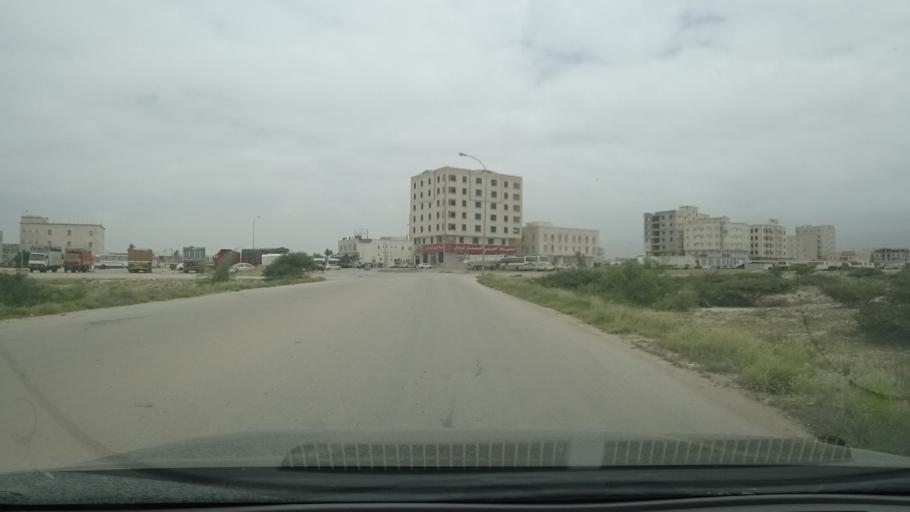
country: OM
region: Zufar
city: Salalah
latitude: 17.0262
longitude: 54.0565
